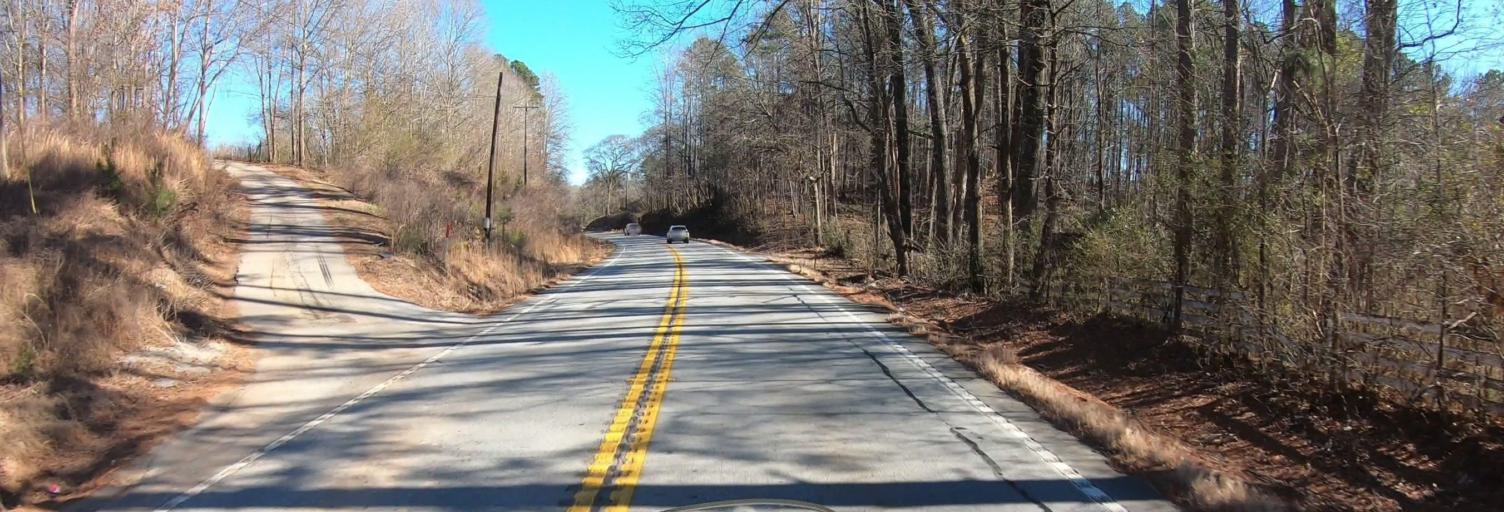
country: US
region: Georgia
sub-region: Stephens County
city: Toccoa
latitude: 34.5924
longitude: -83.2587
